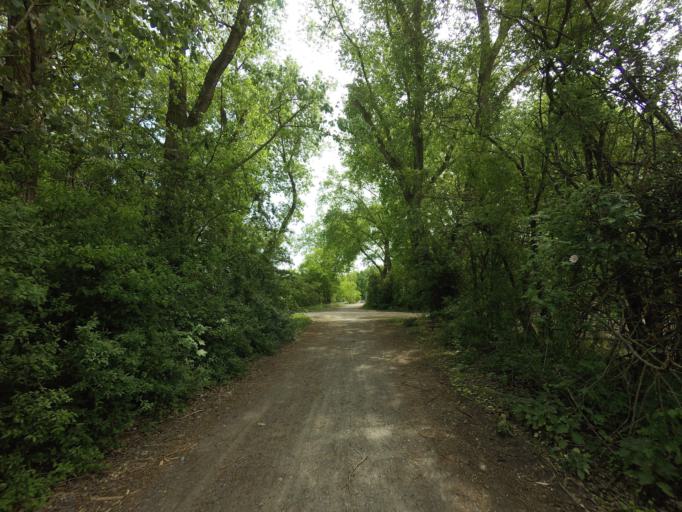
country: DE
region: Lower Saxony
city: Klein Schwulper
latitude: 52.3142
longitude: 10.4717
